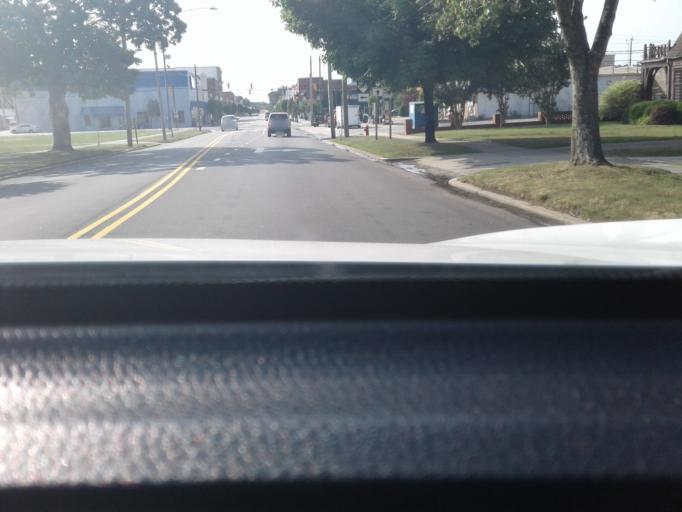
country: US
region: North Carolina
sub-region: Johnston County
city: Benson
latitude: 35.3825
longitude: -78.5499
